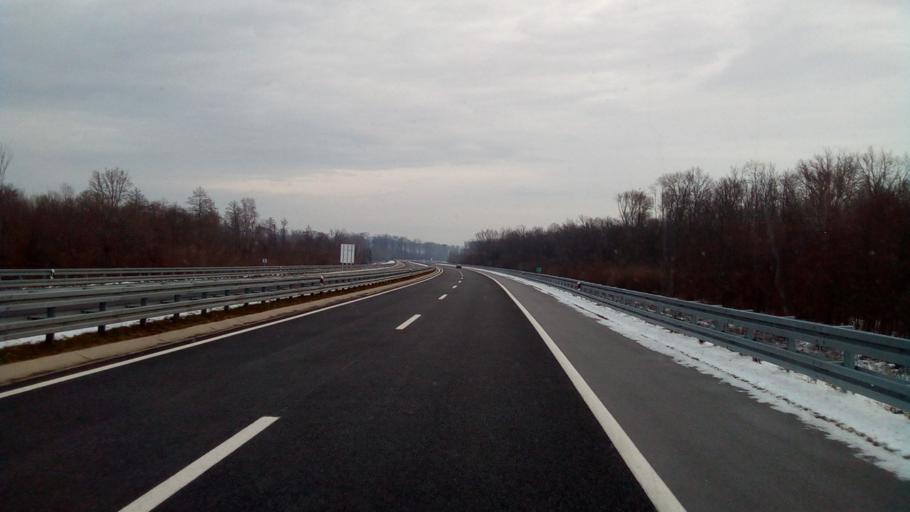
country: HR
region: Sisacko-Moslavacka
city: Lekenik
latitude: 45.5876
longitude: 16.1744
